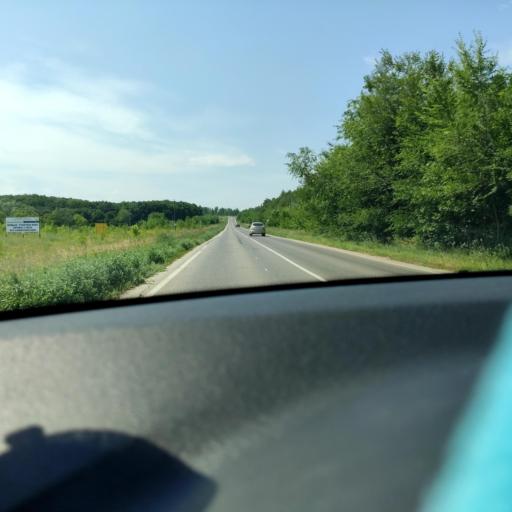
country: RU
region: Samara
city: Petra-Dubrava
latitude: 53.3469
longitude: 50.5057
